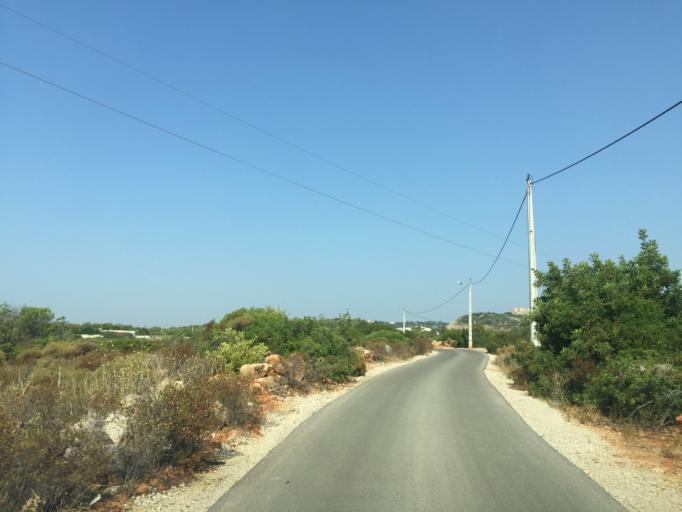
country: PT
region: Faro
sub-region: Loule
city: Almancil
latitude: 37.0946
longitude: -7.9995
